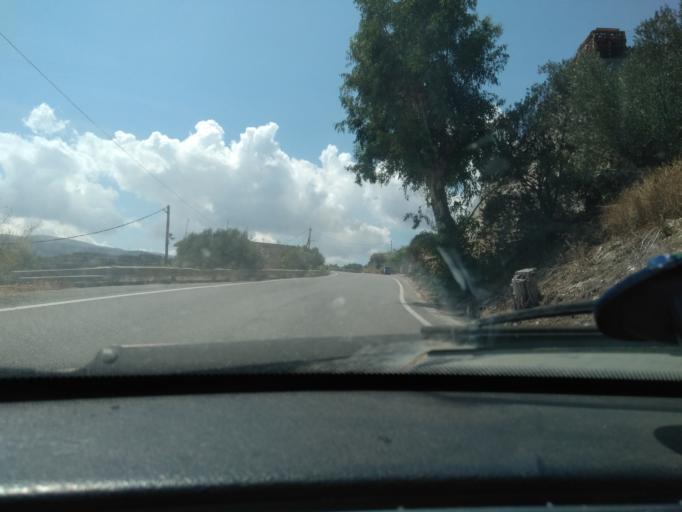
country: GR
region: Crete
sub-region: Nomos Lasithiou
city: Siteia
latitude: 35.1427
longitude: 26.0806
